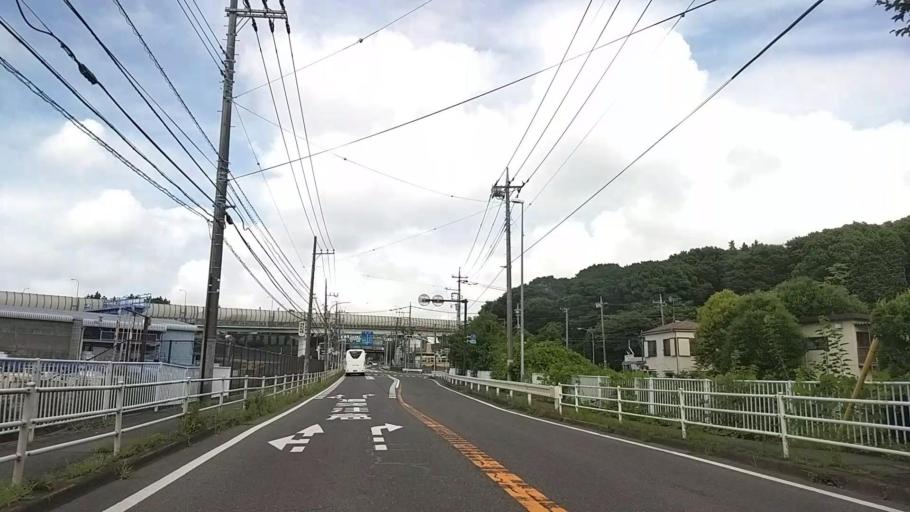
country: JP
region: Kanagawa
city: Minami-rinkan
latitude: 35.4970
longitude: 139.4975
